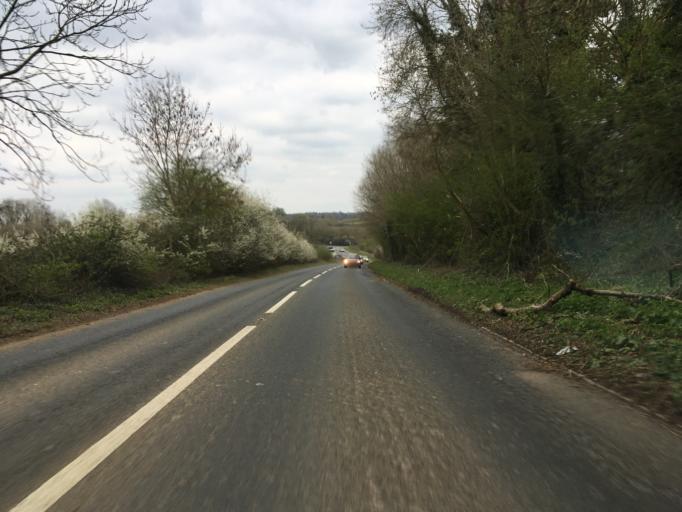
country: GB
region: England
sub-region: Gloucestershire
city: Cirencester
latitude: 51.7300
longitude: -1.9149
